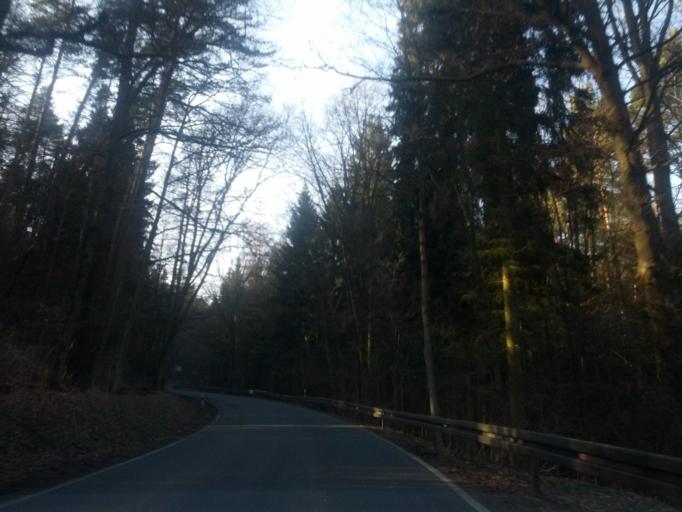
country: DE
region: Thuringia
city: Creuzburg
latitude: 51.0678
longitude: 10.2346
